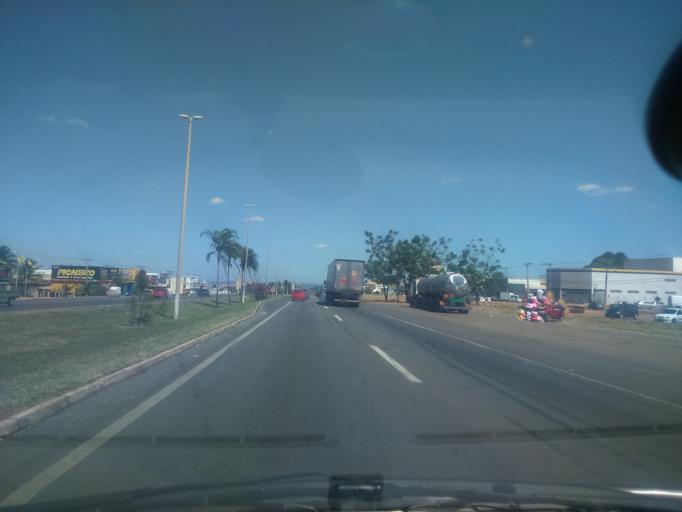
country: BR
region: Goias
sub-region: Luziania
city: Luziania
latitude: -16.0598
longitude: -47.9831
